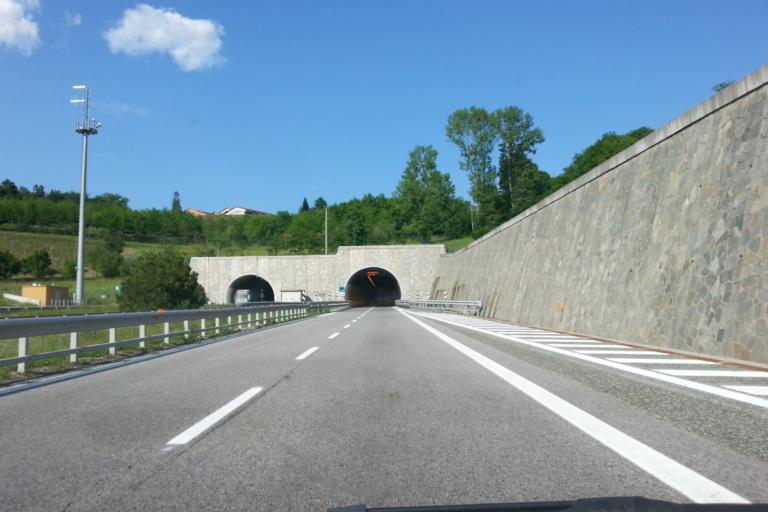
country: IT
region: Piedmont
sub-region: Provincia di Cuneo
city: Briaglia
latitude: 44.4194
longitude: 7.8732
